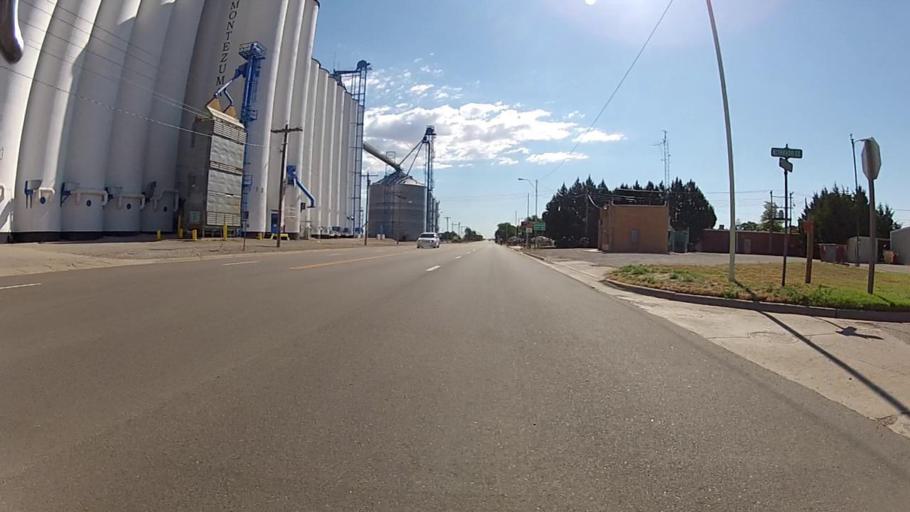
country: US
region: Kansas
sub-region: Gray County
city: Cimarron
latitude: 37.5987
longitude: -100.4441
